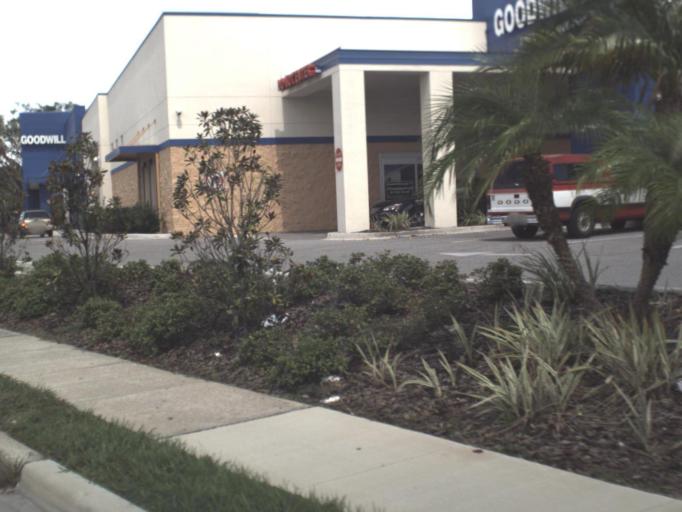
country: US
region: Florida
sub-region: Manatee County
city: Whitfield
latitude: 27.3785
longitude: -82.5555
